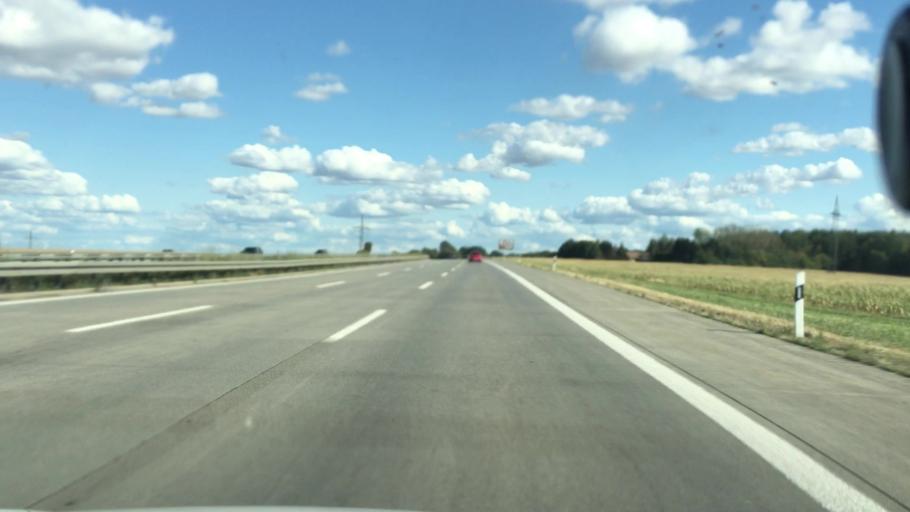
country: DE
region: Thuringia
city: Heyersdorf
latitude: 50.8390
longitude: 12.3598
